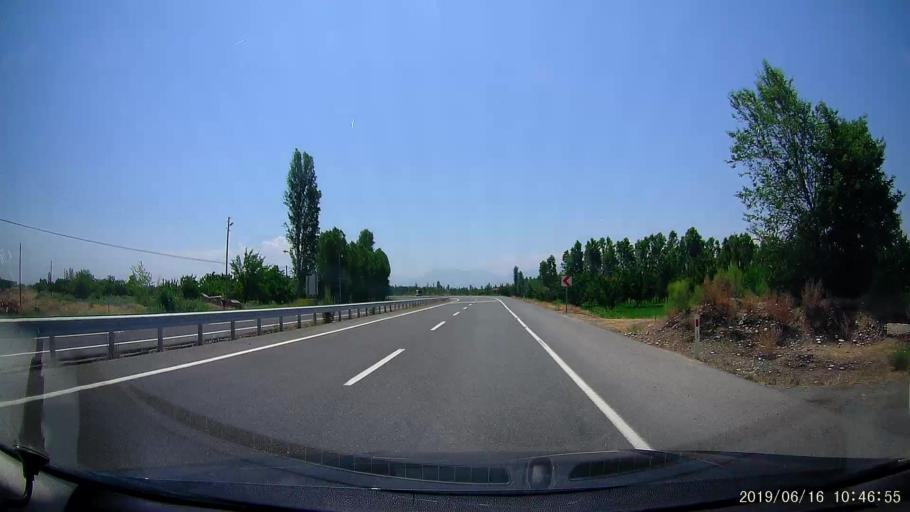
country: AM
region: Armavir
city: Shenavan
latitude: 40.0168
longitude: 43.8826
